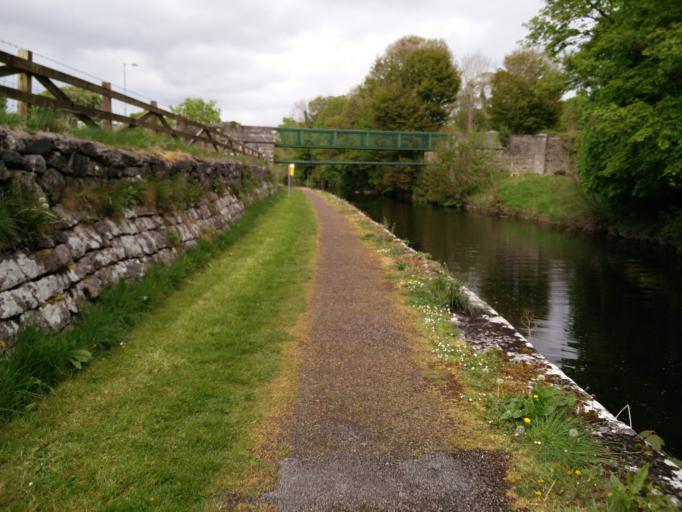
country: IE
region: Connaught
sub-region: Maigh Eo
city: Ballinrobe
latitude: 53.6219
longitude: -9.2257
